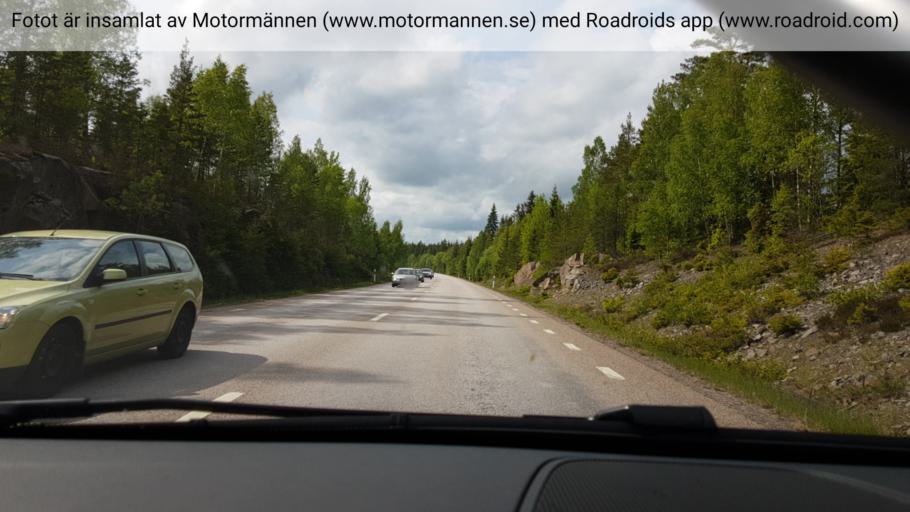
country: SE
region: Uppsala
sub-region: Tierps Kommun
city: Orbyhus
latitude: 60.2056
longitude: 17.7905
